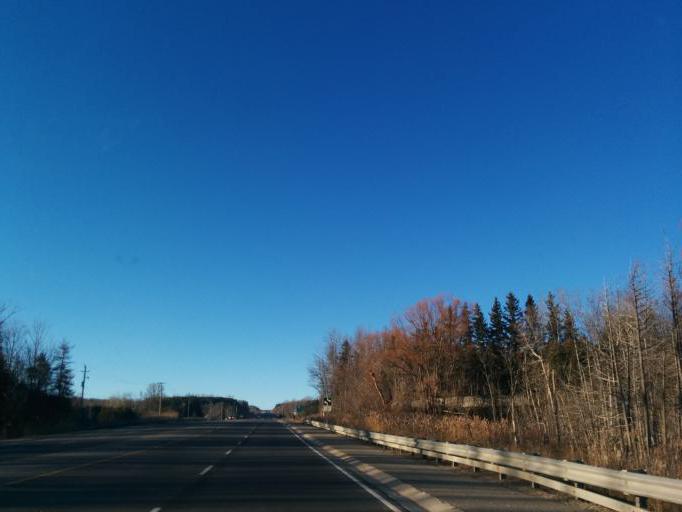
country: CA
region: Ontario
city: Orangeville
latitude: 43.8300
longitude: -79.9547
